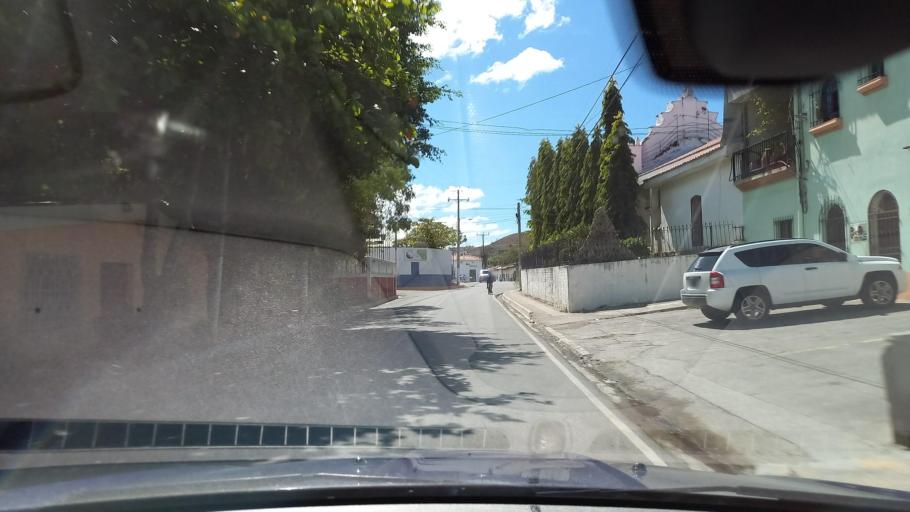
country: SV
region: Santa Ana
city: Metapan
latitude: 14.3370
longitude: -89.4481
